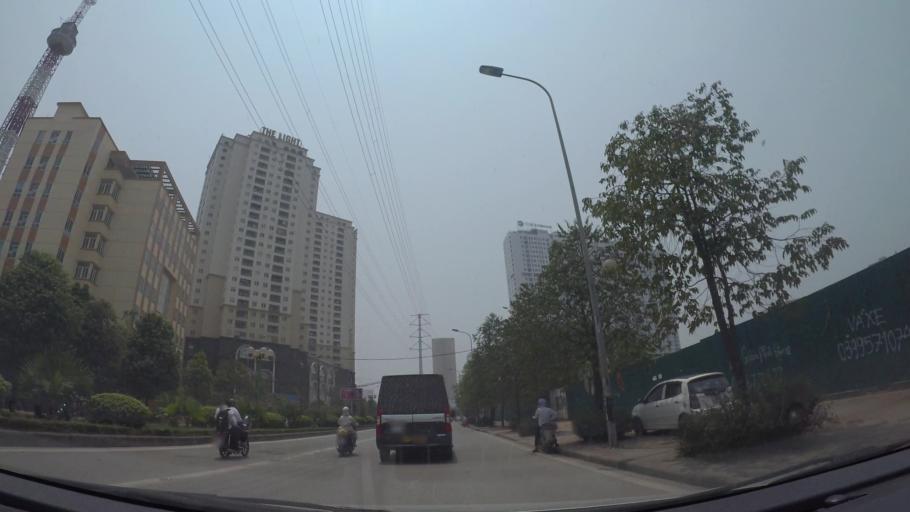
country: VN
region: Ha Noi
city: Thanh Xuan
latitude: 20.9943
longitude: 105.7893
